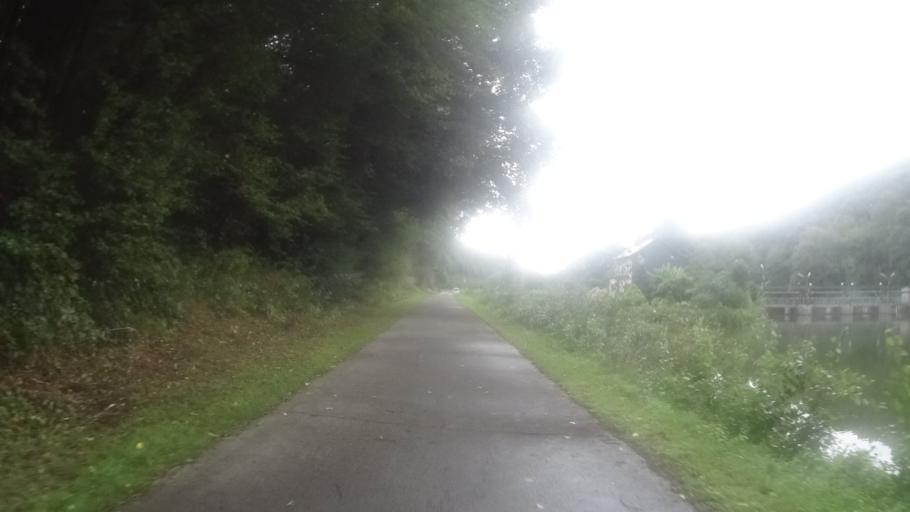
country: BE
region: Wallonia
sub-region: Province du Hainaut
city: Thuin
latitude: 50.3481
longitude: 4.3085
